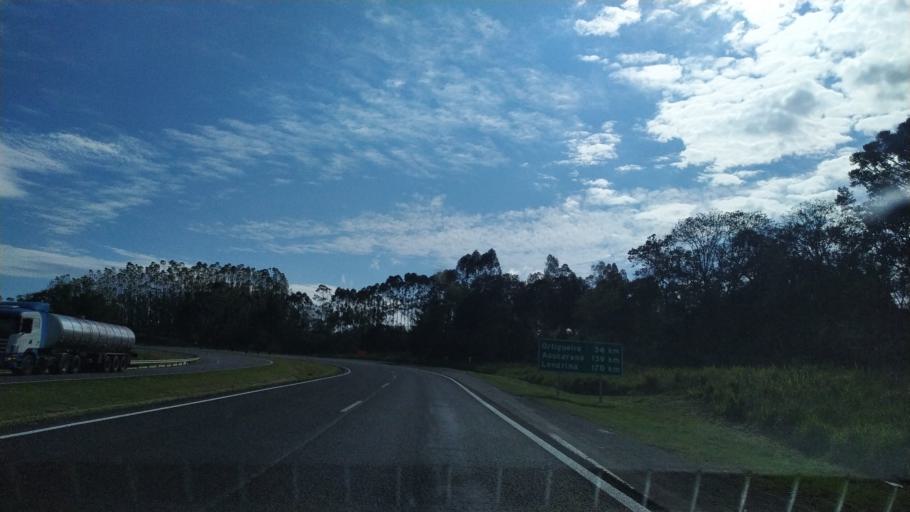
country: BR
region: Parana
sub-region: Telemaco Borba
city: Telemaco Borba
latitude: -24.4291
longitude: -50.7660
